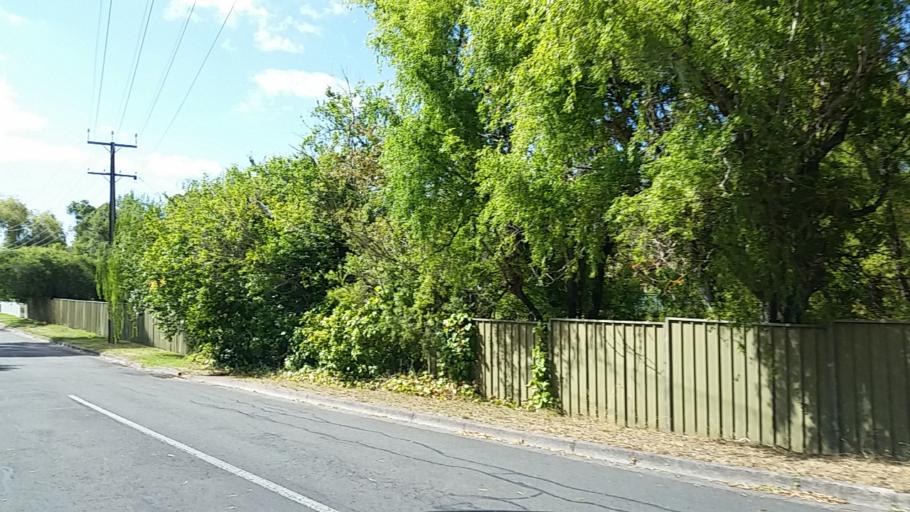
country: AU
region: South Australia
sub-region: Mount Barker
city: Hahndorf
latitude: -35.0303
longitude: 138.8175
